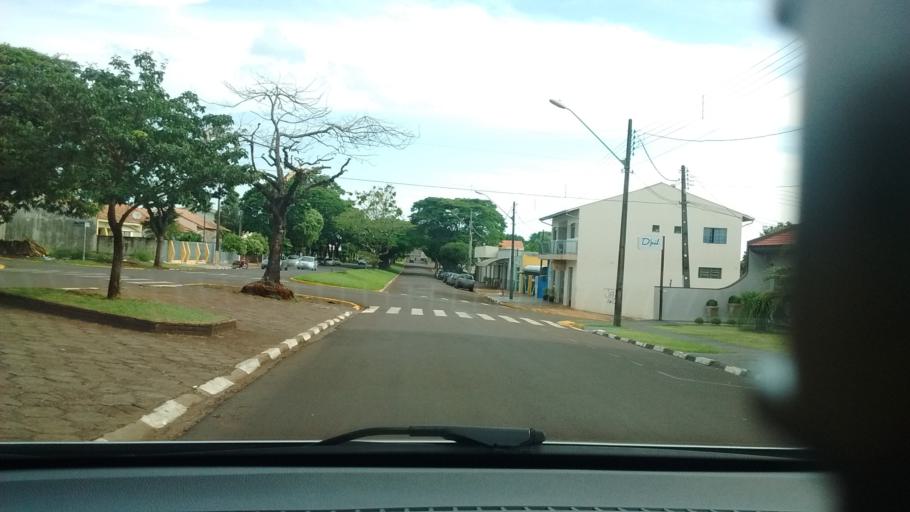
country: BR
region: Parana
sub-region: Corbelia
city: Corbelia
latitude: -24.5479
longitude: -52.9895
